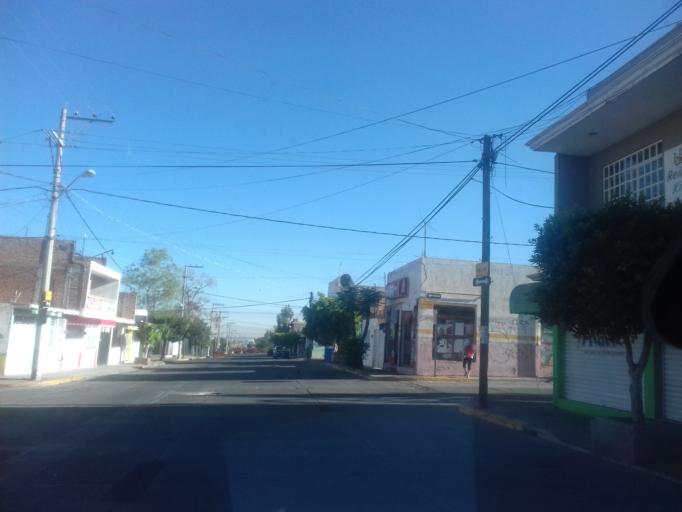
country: MX
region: Aguascalientes
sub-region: Aguascalientes
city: San Sebastian [Fraccionamiento]
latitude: 21.8516
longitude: -102.2648
